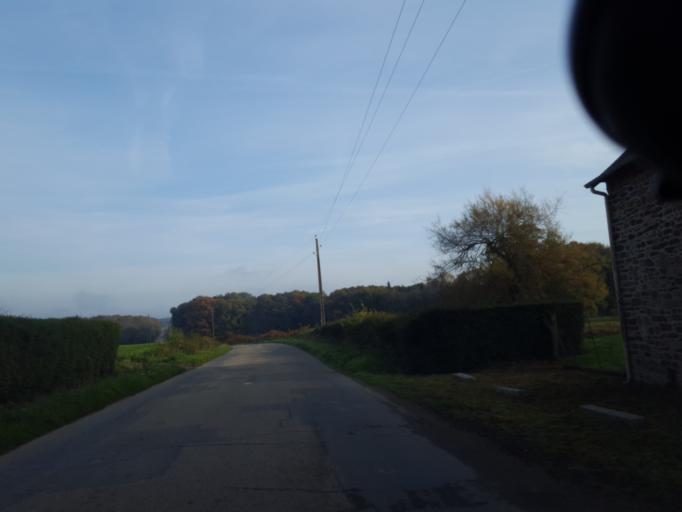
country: FR
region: Brittany
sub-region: Departement d'Ille-et-Vilaine
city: Guignen
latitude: 47.9192
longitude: -1.8490
